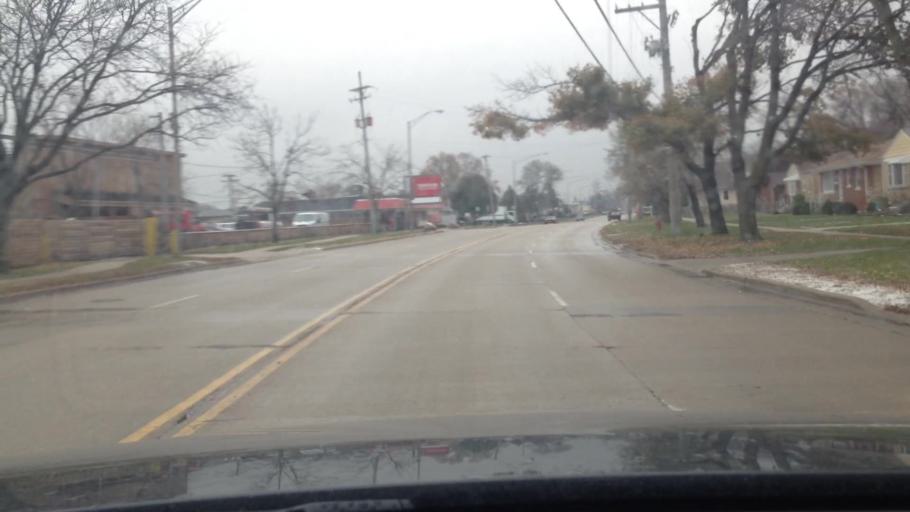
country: US
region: Illinois
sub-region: Cook County
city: Schiller Park
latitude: 41.9596
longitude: -87.8711
